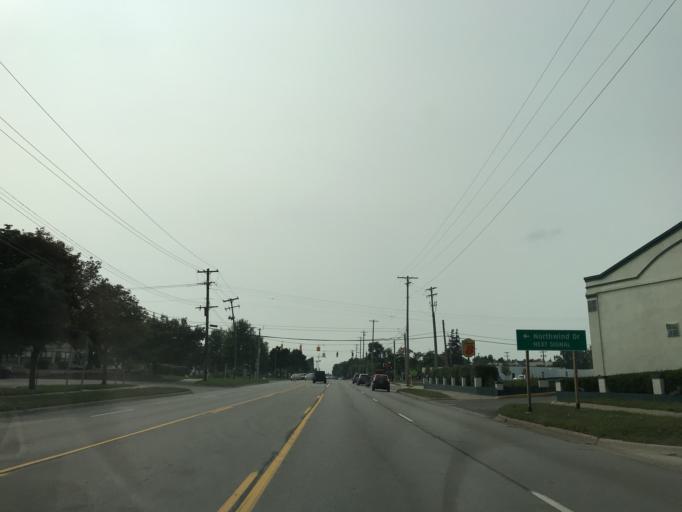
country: US
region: Michigan
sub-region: Ingham County
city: Okemos
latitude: 42.7264
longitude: -84.4516
